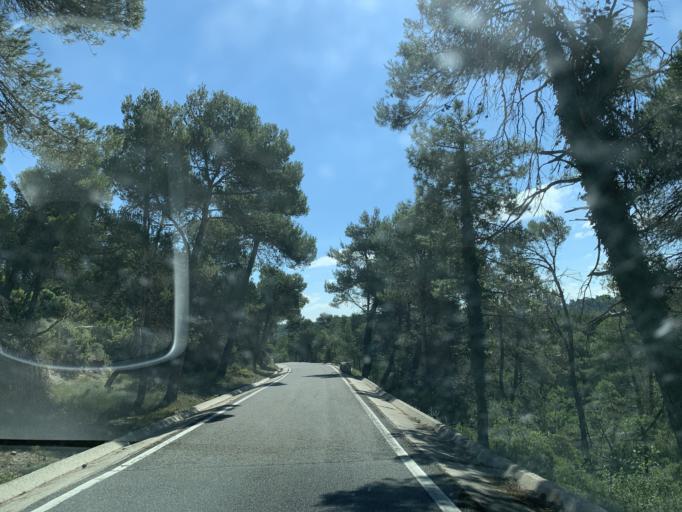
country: ES
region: Catalonia
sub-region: Provincia de Tarragona
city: Conesa
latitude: 41.5409
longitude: 1.3172
